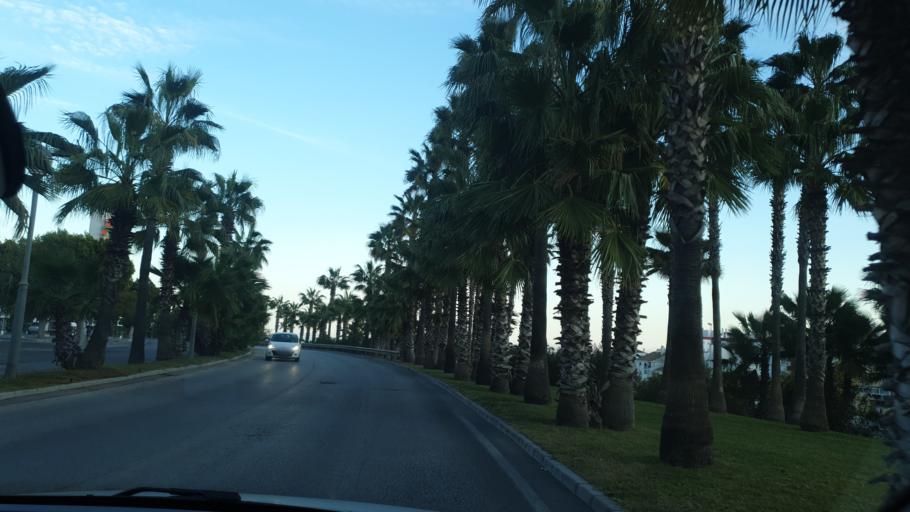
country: ES
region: Andalusia
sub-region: Provincia de Malaga
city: Marbella
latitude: 36.5212
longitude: -4.8785
